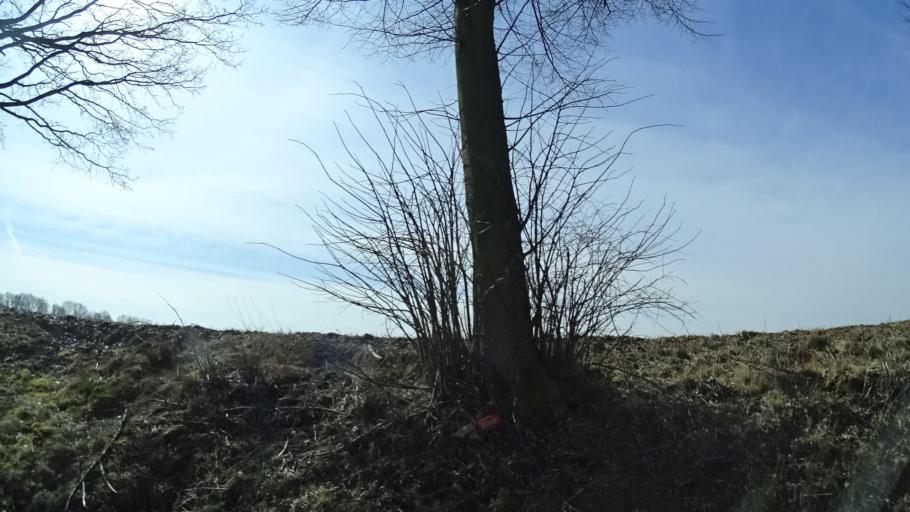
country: DE
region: Hesse
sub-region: Regierungsbezirk Giessen
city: Grunberg
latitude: 50.6257
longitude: 9.0198
